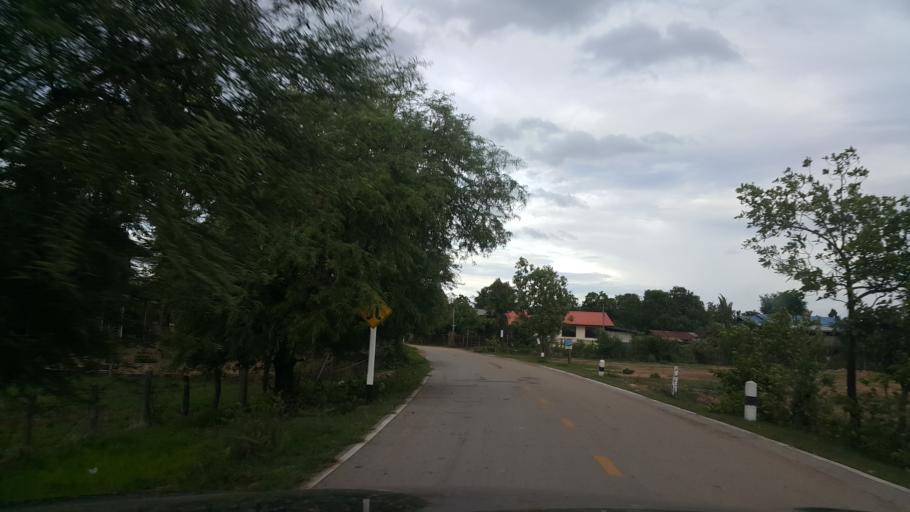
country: TH
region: Sukhothai
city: Ban Dan Lan Hoi
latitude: 17.1551
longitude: 99.5148
